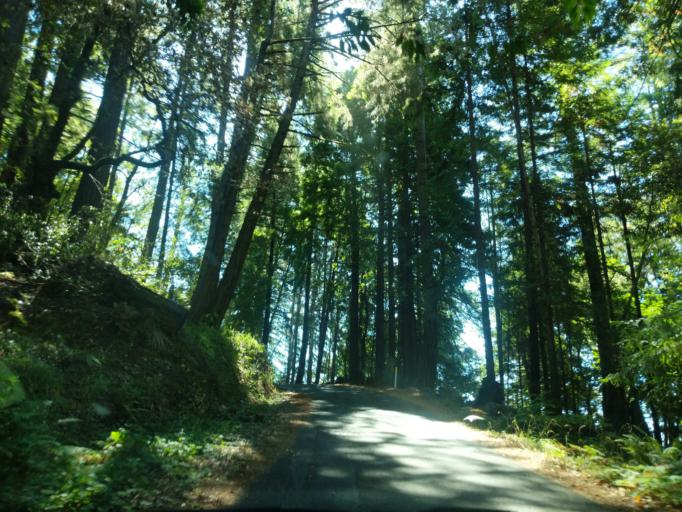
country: US
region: California
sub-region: Sonoma County
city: Monte Rio
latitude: 38.5248
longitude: -123.2391
